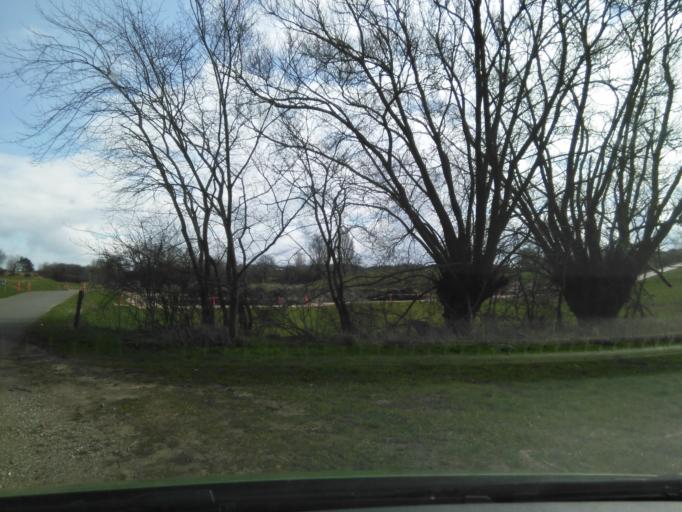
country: DK
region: South Denmark
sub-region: Middelfart Kommune
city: Strib
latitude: 55.5441
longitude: 9.7955
